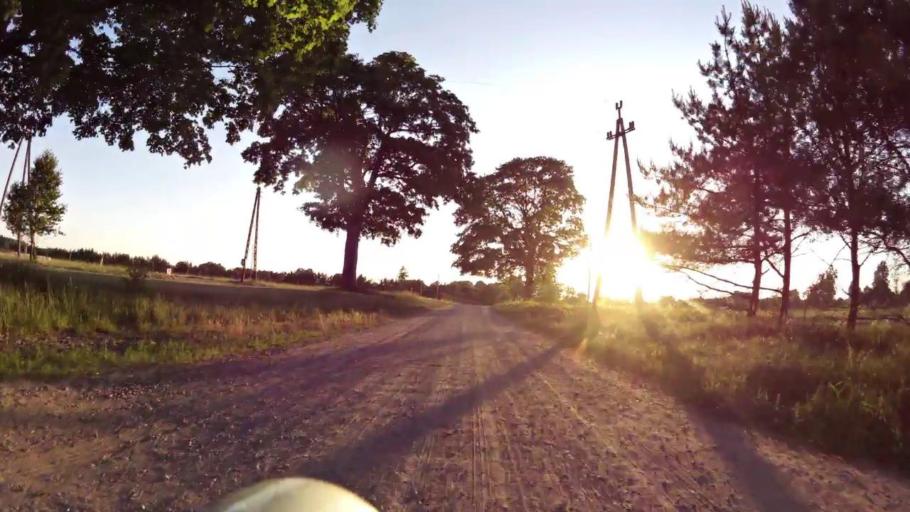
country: PL
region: West Pomeranian Voivodeship
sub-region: Powiat szczecinecki
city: Szczecinek
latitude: 53.8444
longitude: 16.6858
